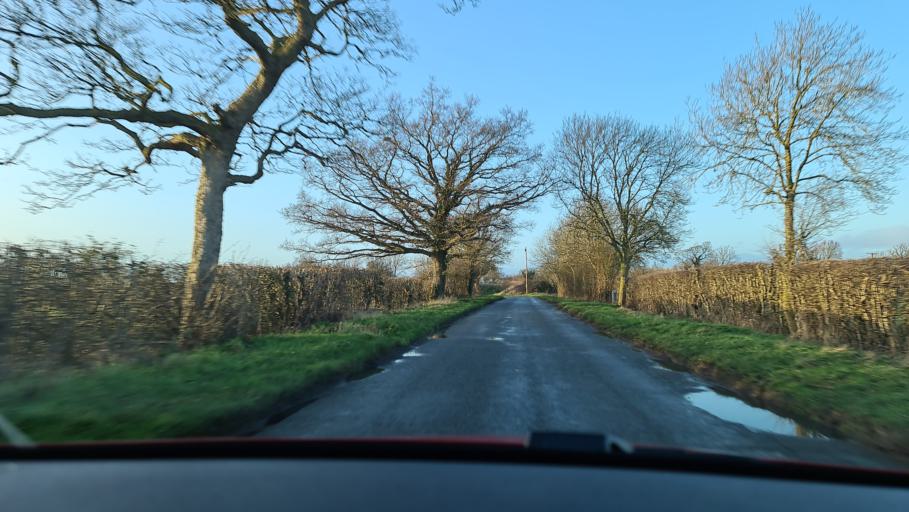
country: GB
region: England
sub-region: Northamptonshire
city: Deanshanger
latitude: 52.0518
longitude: -0.8695
